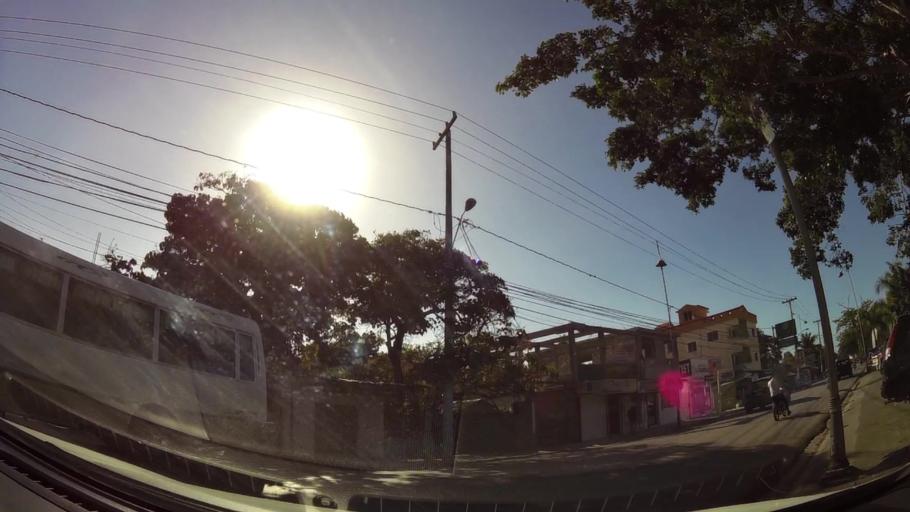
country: DO
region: Santo Domingo
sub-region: Santo Domingo
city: Boca Chica
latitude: 18.4527
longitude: -69.6057
